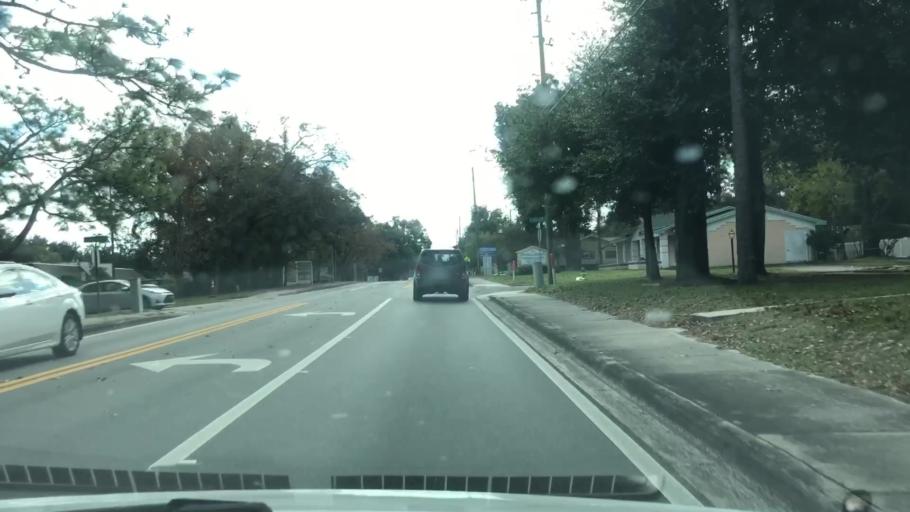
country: US
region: Florida
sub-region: Seminole County
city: Altamonte Springs
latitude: 28.6758
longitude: -81.3739
